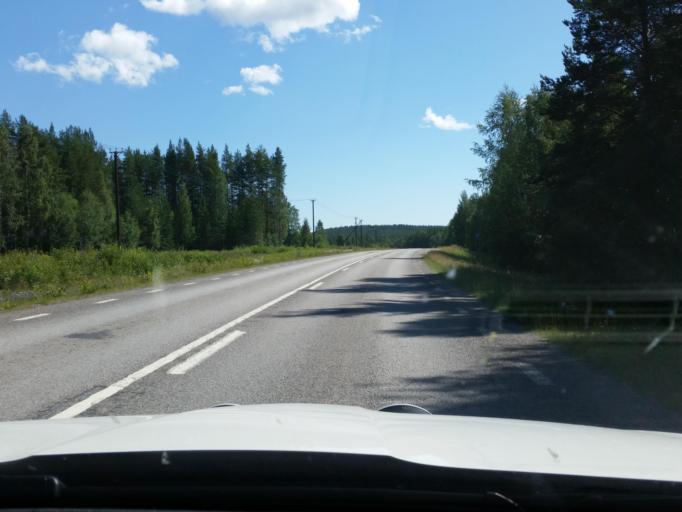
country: SE
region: Norrbotten
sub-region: Alvsbyns Kommun
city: AElvsbyn
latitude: 65.6923
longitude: 20.6818
